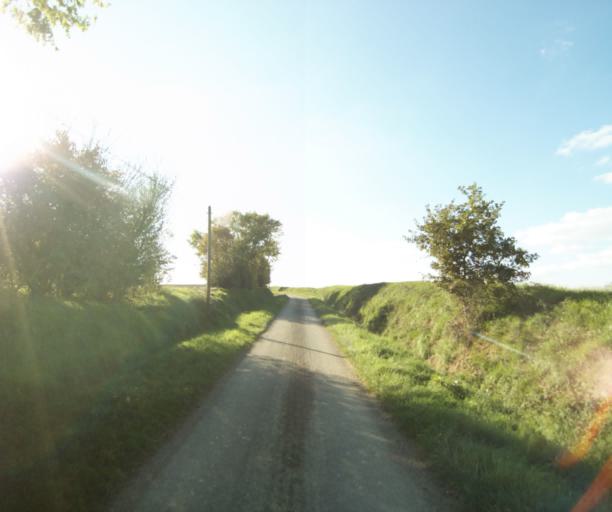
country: FR
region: Midi-Pyrenees
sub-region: Departement du Gers
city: Eauze
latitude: 43.7635
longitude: 0.1515
